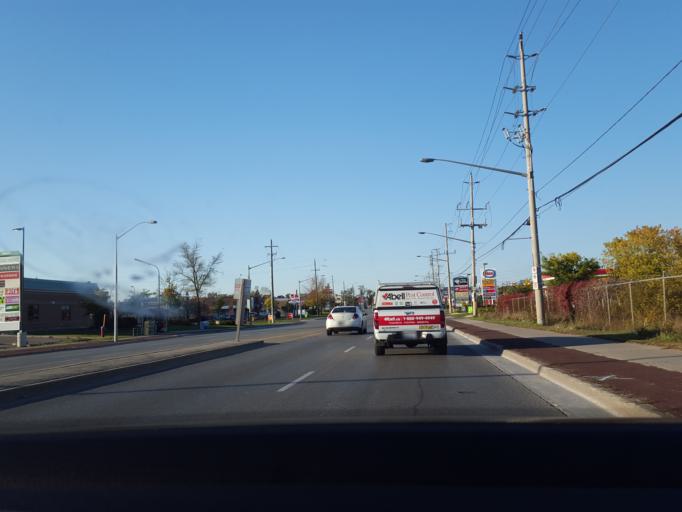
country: CA
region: Ontario
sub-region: York
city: Richmond Hill
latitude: 43.8844
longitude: -79.4402
